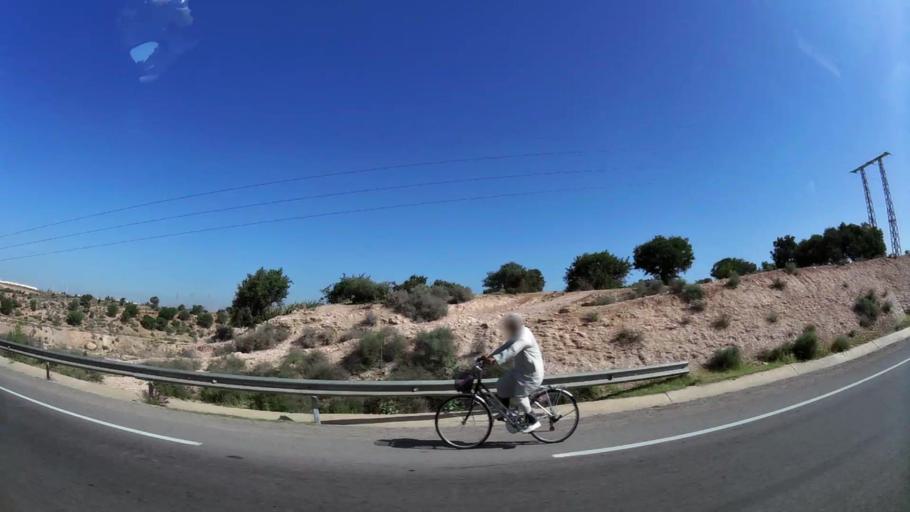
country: MA
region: Souss-Massa-Draa
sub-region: Inezgane-Ait Mellou
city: Inezgane
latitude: 30.3858
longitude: -9.4907
